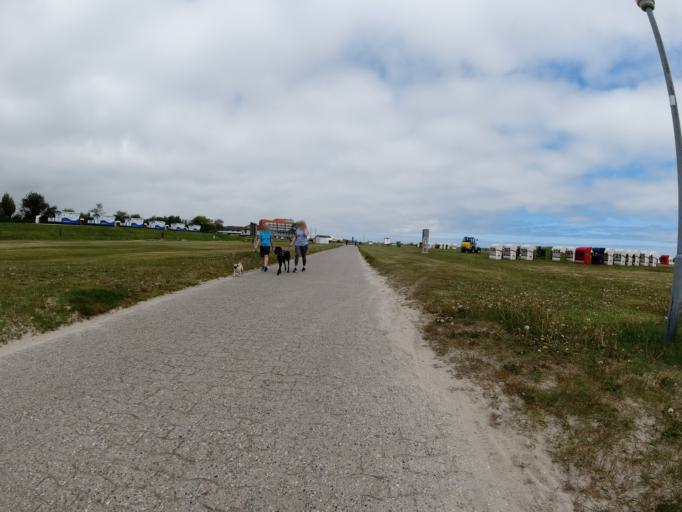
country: DE
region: Lower Saxony
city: Schillig
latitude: 53.7012
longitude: 8.0289
